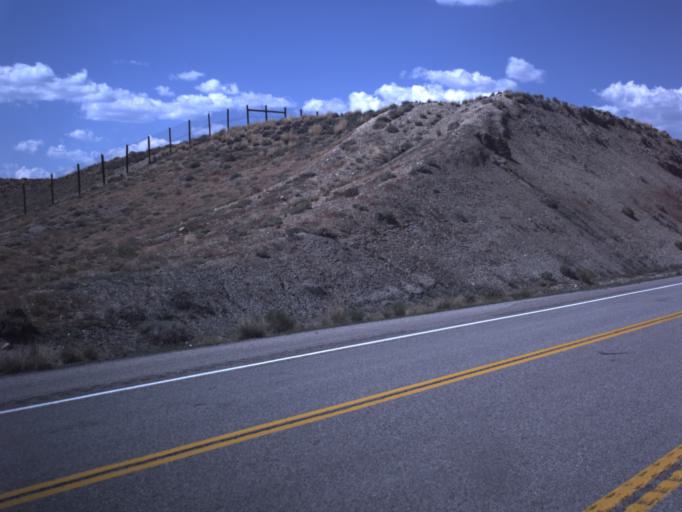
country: US
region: Utah
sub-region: Emery County
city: Huntington
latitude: 39.4349
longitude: -110.8671
